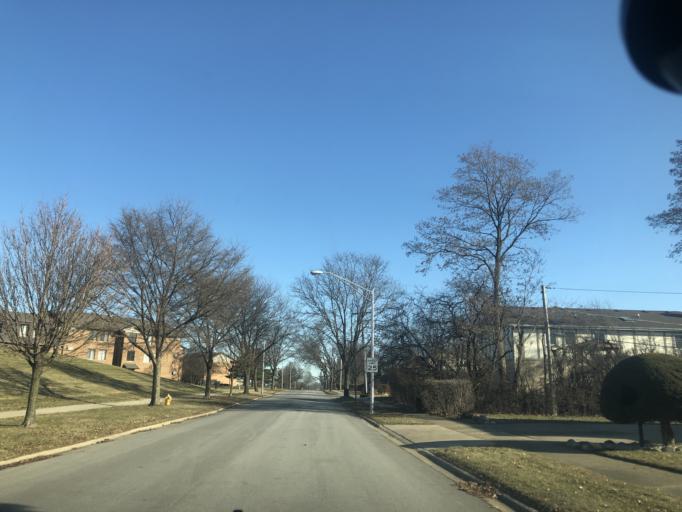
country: US
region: Illinois
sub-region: DuPage County
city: Addison
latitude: 41.9361
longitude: -88.0075
